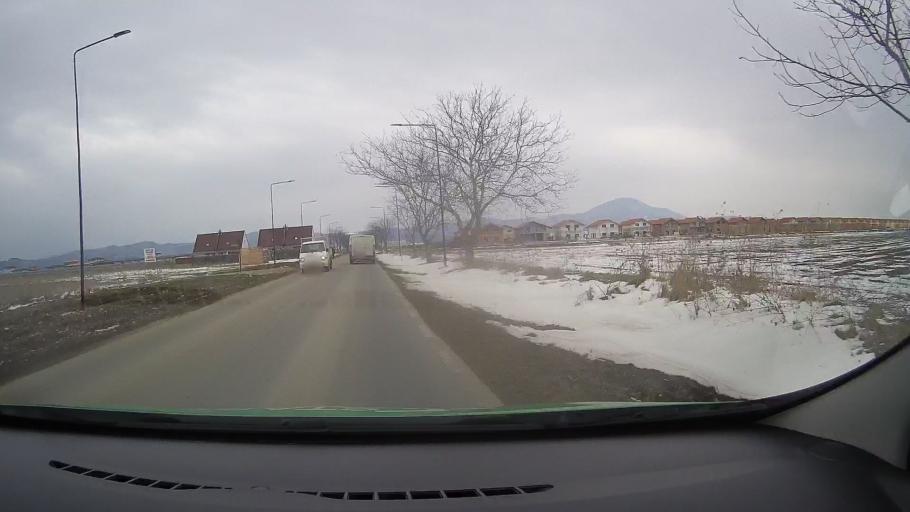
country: RO
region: Brasov
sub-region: Comuna Cristian
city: Cristian
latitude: 45.6288
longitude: 25.4675
